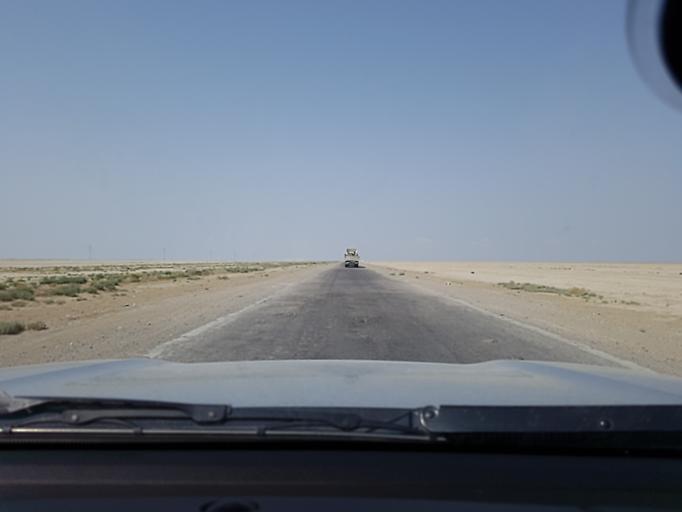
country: TM
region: Balkan
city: Gumdag
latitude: 38.7320
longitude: 54.5008
